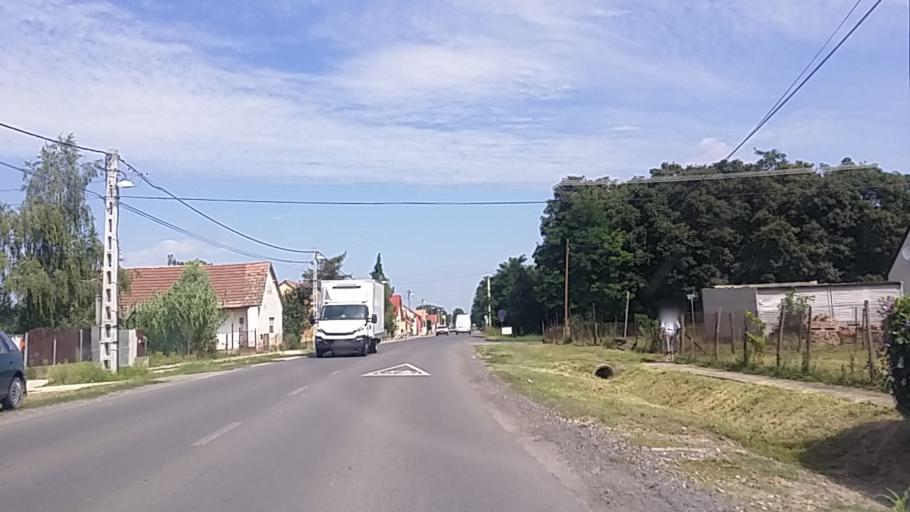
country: HU
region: Tolna
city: Dombovar
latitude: 46.3335
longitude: 18.1270
